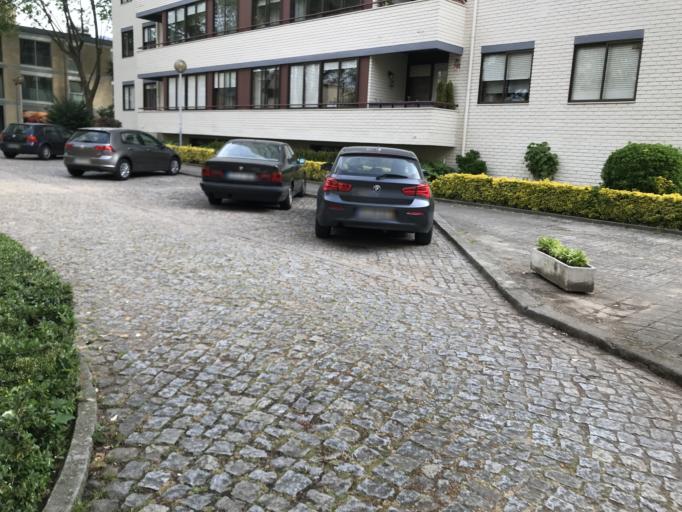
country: PT
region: Porto
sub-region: Matosinhos
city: Senhora da Hora
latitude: 41.1816
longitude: -8.6698
